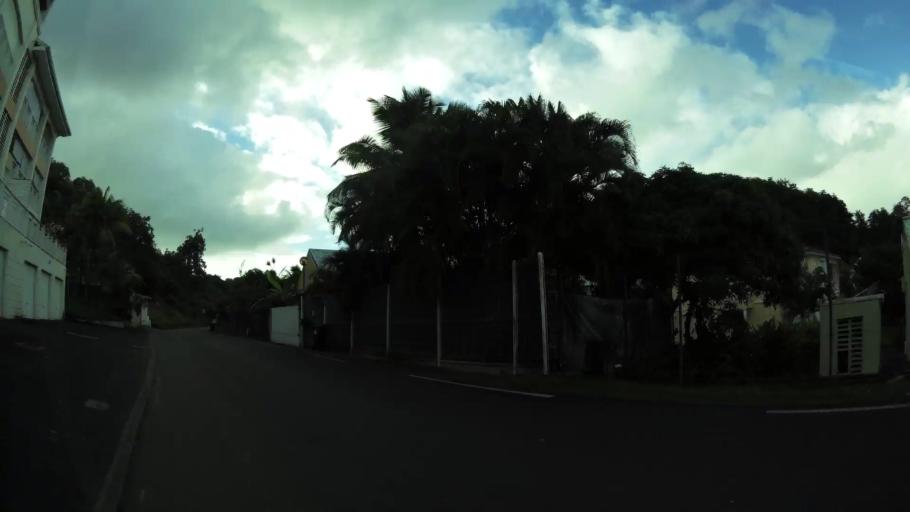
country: GP
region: Guadeloupe
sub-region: Guadeloupe
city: Pointe-a-Pitre
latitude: 16.2483
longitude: -61.5173
